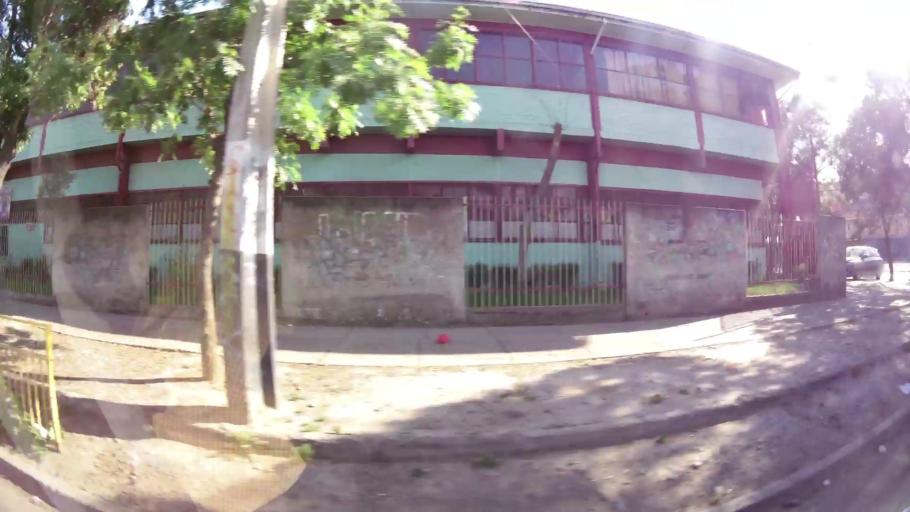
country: CL
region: Santiago Metropolitan
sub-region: Provincia de Santiago
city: Lo Prado
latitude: -33.4240
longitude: -70.7478
